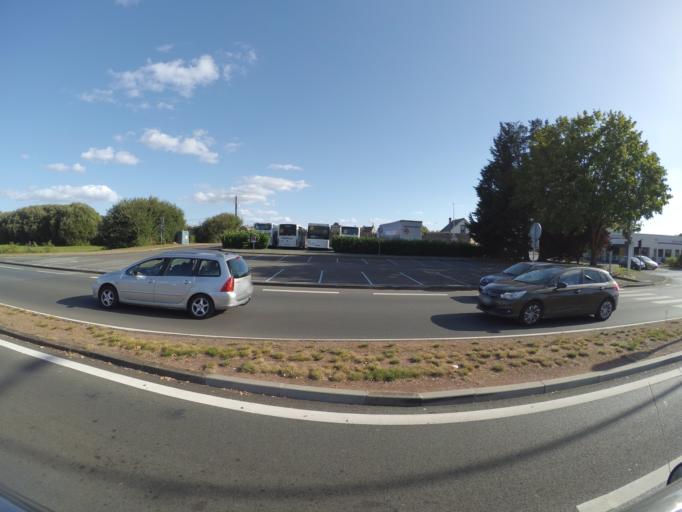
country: FR
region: Pays de la Loire
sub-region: Departement de Maine-et-Loire
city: Cholet
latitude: 47.0527
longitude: -0.8689
